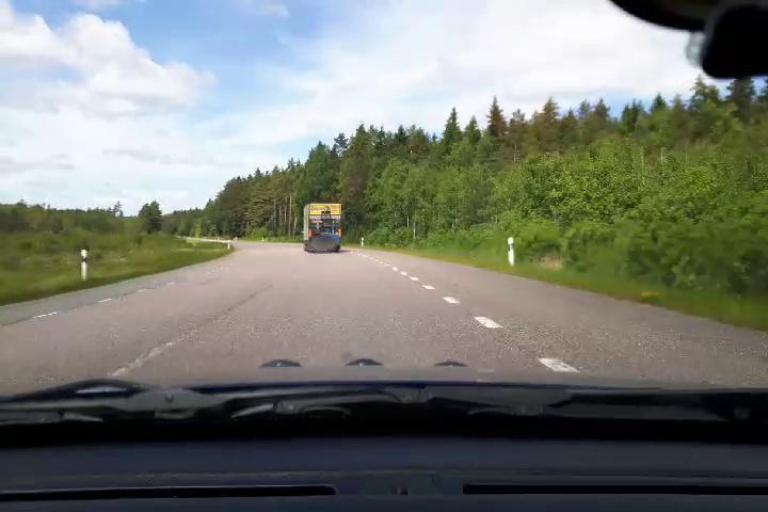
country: SE
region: Uppsala
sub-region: Osthammars Kommun
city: Bjorklinge
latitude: 60.1000
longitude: 17.5532
